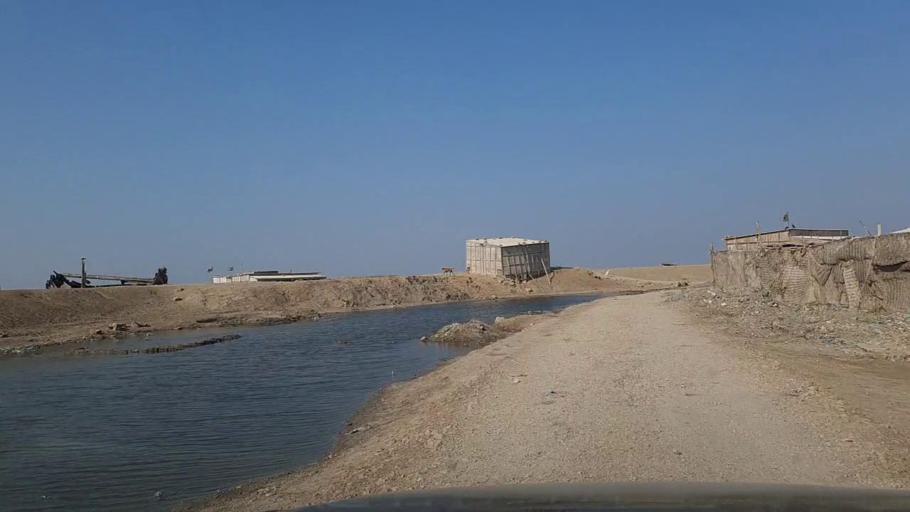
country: PK
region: Sindh
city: Keti Bandar
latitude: 24.1450
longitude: 67.4496
